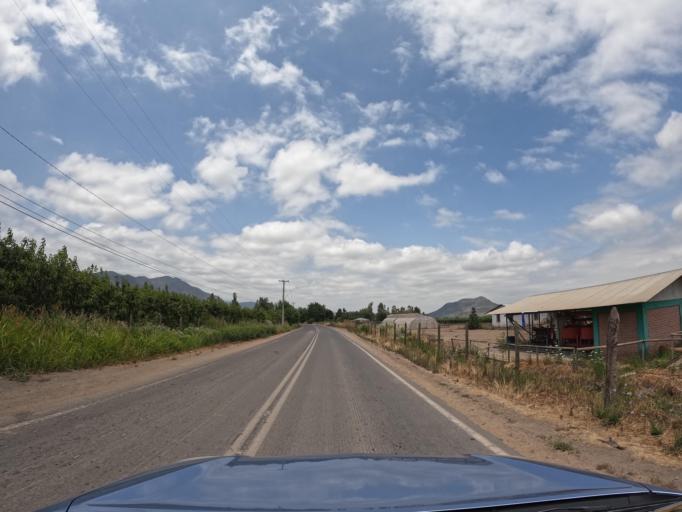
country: CL
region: O'Higgins
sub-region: Provincia de Colchagua
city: Chimbarongo
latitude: -34.7557
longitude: -70.9539
